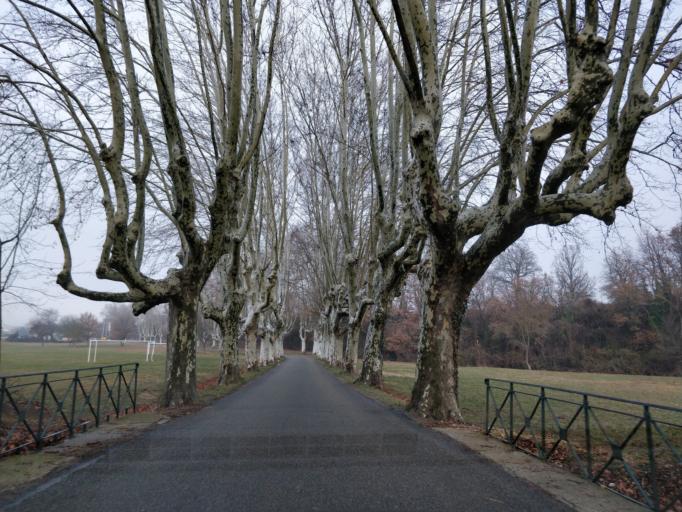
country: FR
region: Languedoc-Roussillon
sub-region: Departement du Gard
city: Saint-Mamert-du-Gard
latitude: 43.8990
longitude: 4.2120
